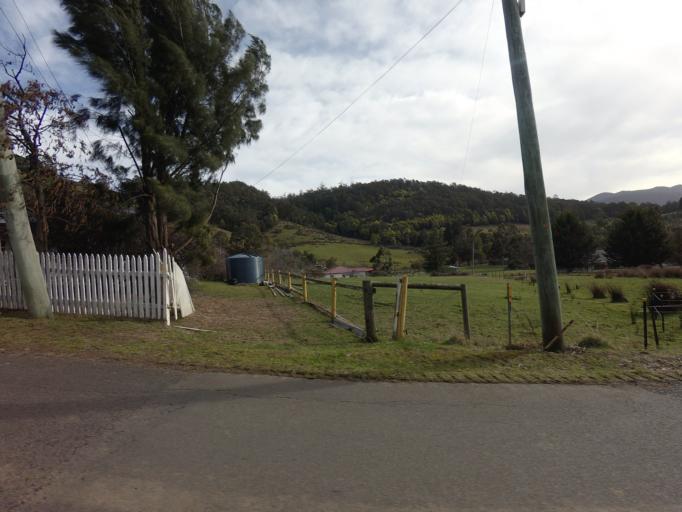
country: AU
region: Tasmania
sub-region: Kingborough
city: Margate
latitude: -42.9944
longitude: 147.1832
